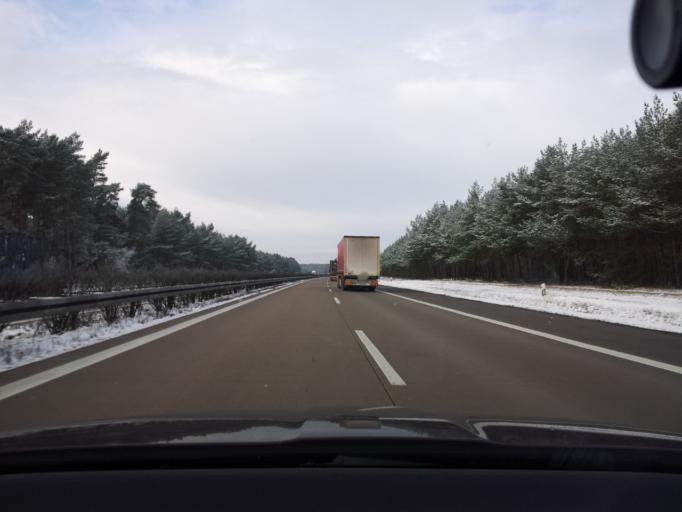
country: DE
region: Mecklenburg-Vorpommern
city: Rastow
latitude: 53.4301
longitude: 11.4324
